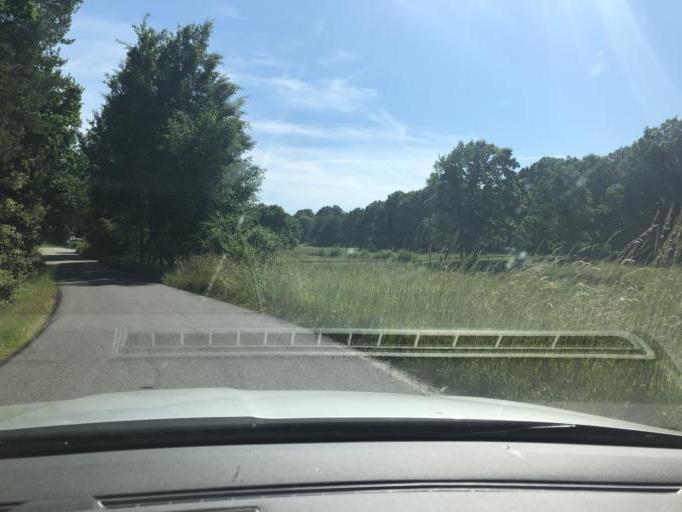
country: SE
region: Blekinge
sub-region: Karlshamns Kommun
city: Morrum
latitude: 56.1639
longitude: 14.8031
